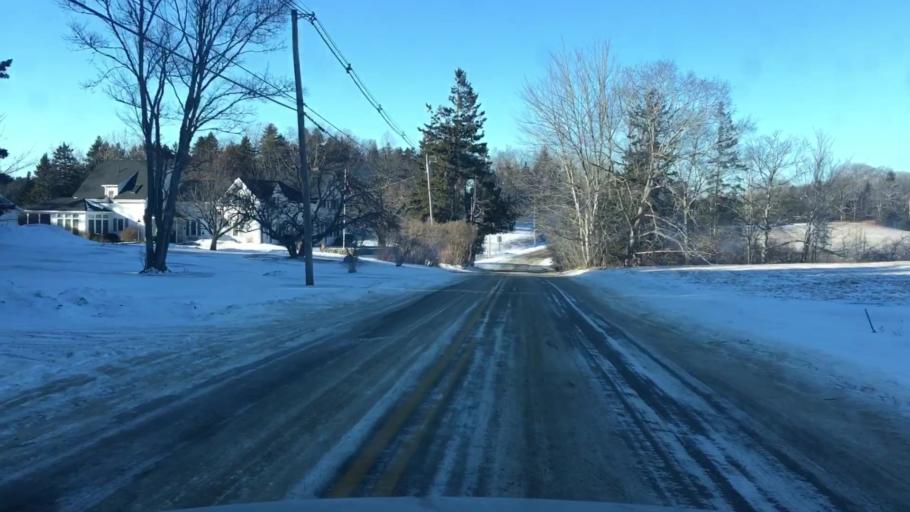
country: US
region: Maine
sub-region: Hancock County
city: Castine
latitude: 44.3464
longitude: -68.7463
